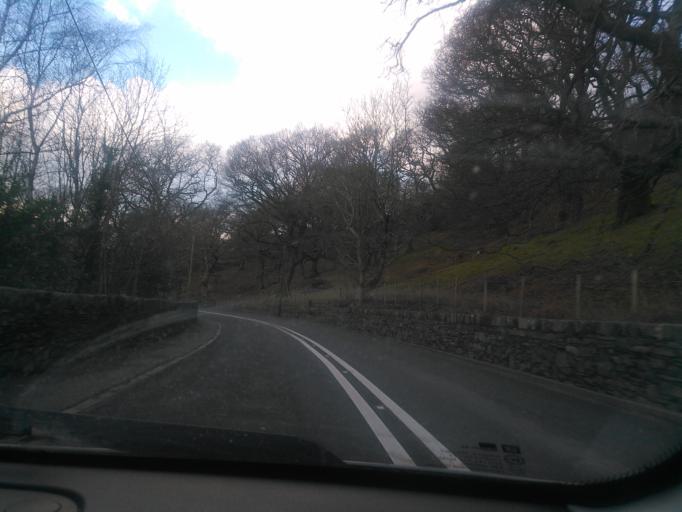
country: GB
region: Wales
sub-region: Gwynedd
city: Bethesda
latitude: 53.1665
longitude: -4.0495
